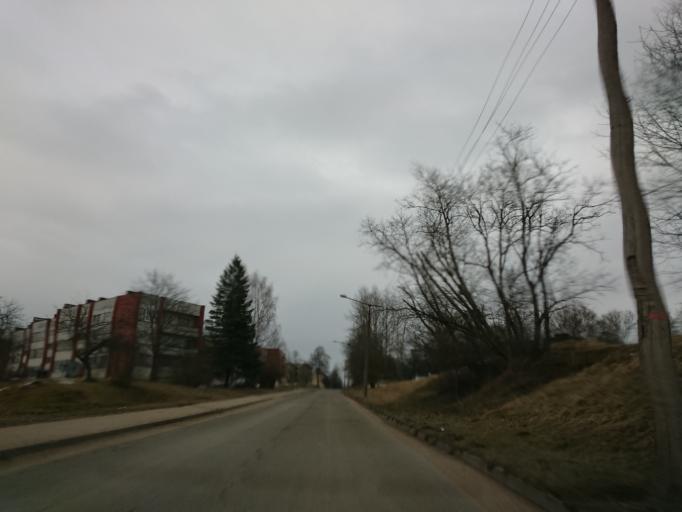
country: LV
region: Cesu Rajons
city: Cesis
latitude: 57.3222
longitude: 25.2601
